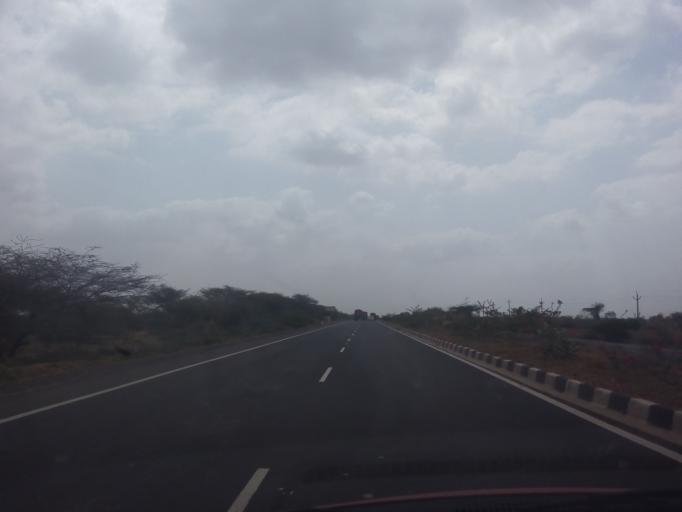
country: IN
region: Gujarat
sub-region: Surendranagar
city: Halvad
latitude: 23.0143
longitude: 71.2806
